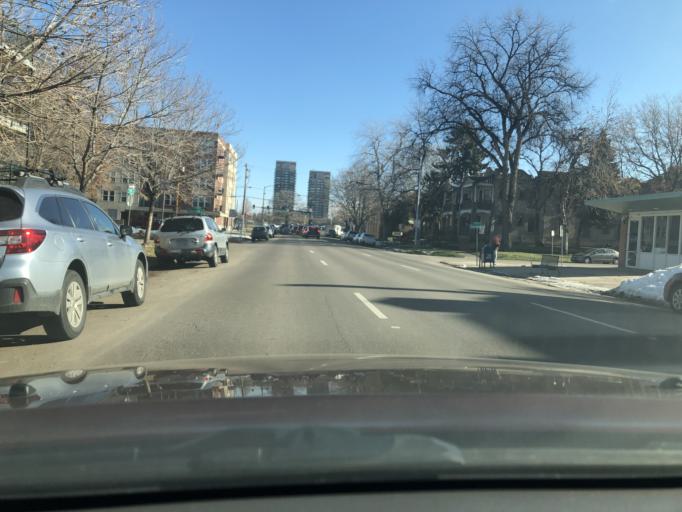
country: US
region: Colorado
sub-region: Denver County
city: Denver
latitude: 39.7432
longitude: -104.9616
